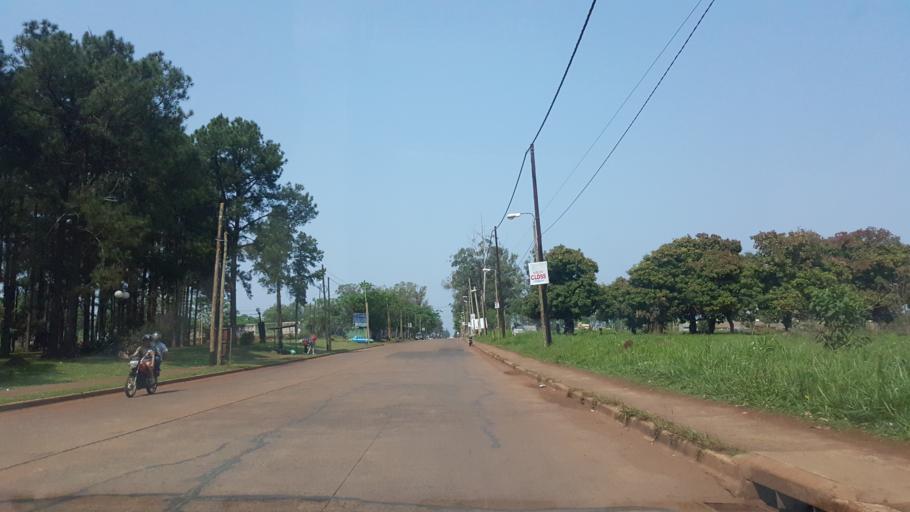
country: AR
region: Misiones
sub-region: Departamento de Capital
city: Posadas
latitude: -27.4027
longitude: -55.9526
